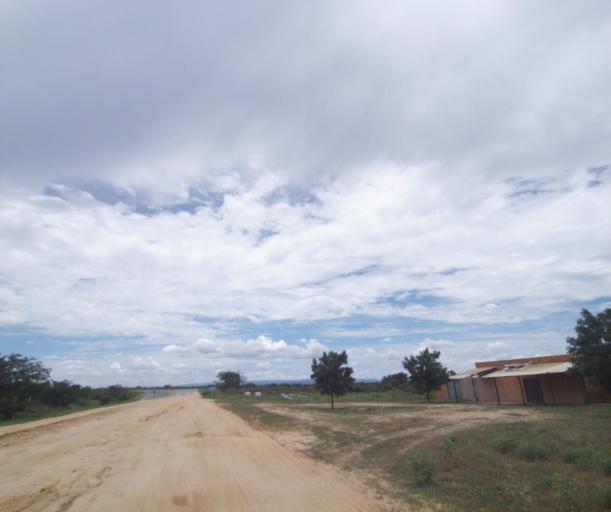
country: BR
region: Bahia
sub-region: Carinhanha
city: Carinhanha
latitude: -14.2861
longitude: -43.7856
